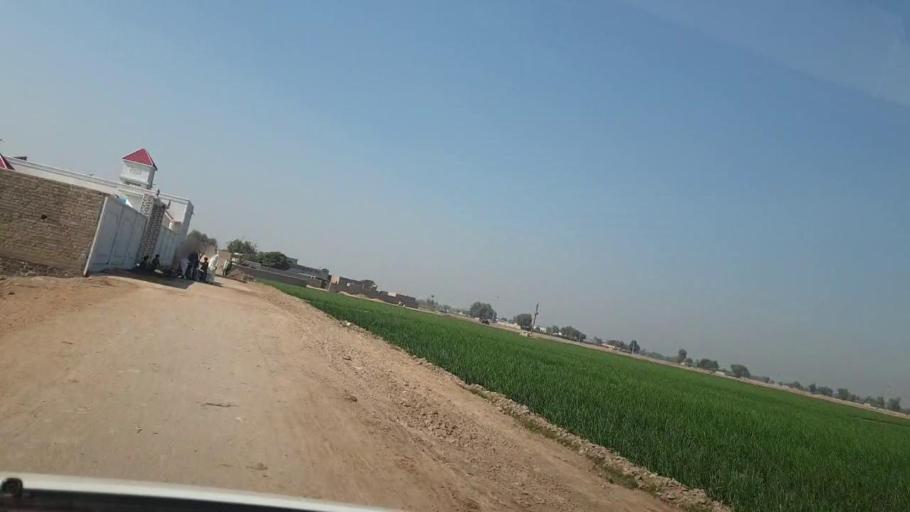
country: PK
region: Sindh
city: Bhan
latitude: 26.6455
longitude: 67.7030
